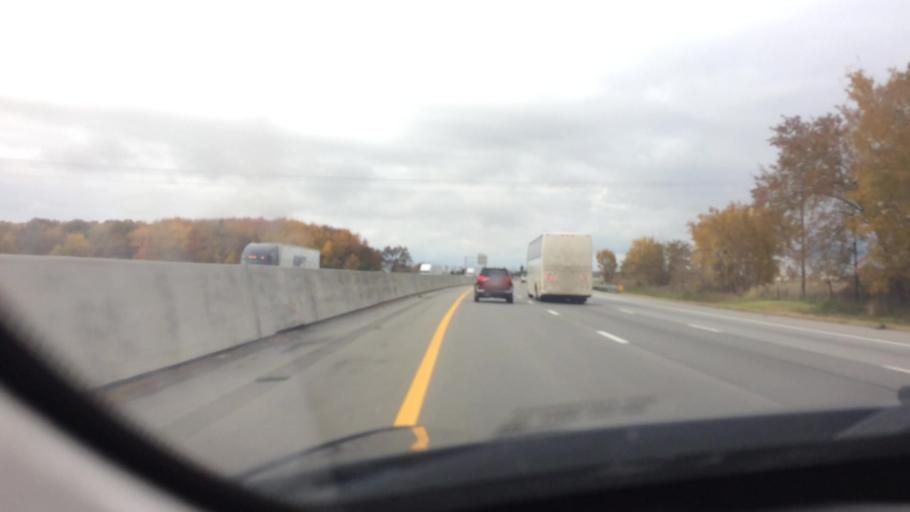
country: US
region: Ohio
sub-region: Wood County
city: North Baltimore
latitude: 41.1525
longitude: -83.6578
